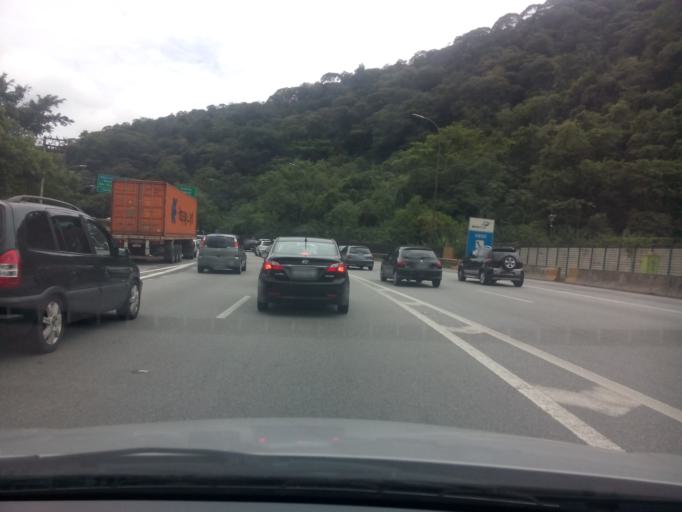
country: BR
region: Sao Paulo
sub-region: Cubatao
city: Cubatao
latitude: -23.8915
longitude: -46.4413
